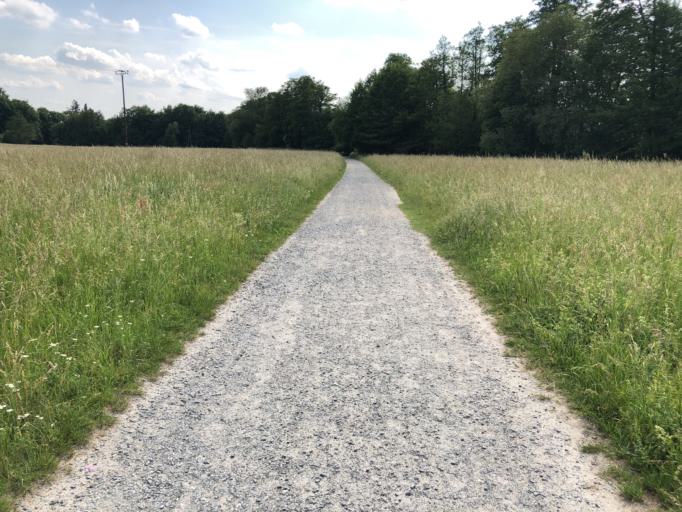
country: DE
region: Hesse
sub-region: Regierungsbezirk Darmstadt
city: Konigstein im Taunus
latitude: 50.1748
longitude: 8.4597
